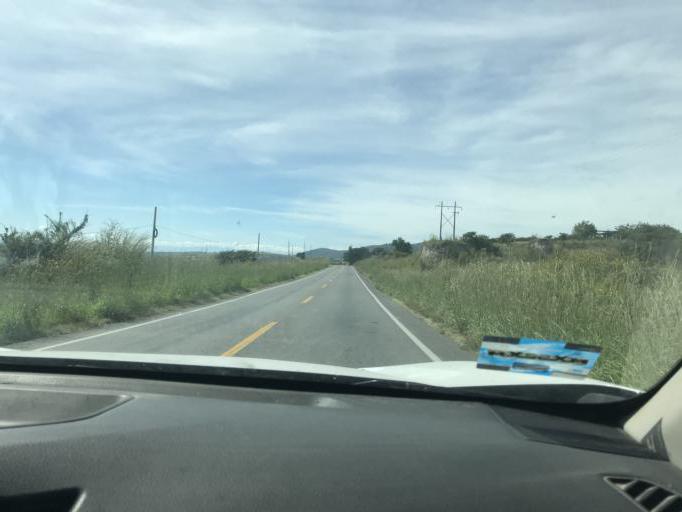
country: MX
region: Guerrero
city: Tepecoacuilco de Trujano
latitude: 18.2817
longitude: -99.5138
